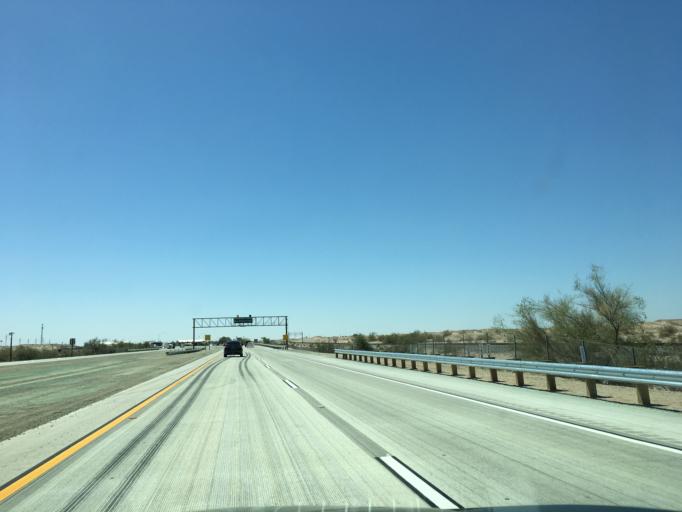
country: MX
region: Baja California
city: Los Algodones
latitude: 32.7455
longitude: -114.7339
